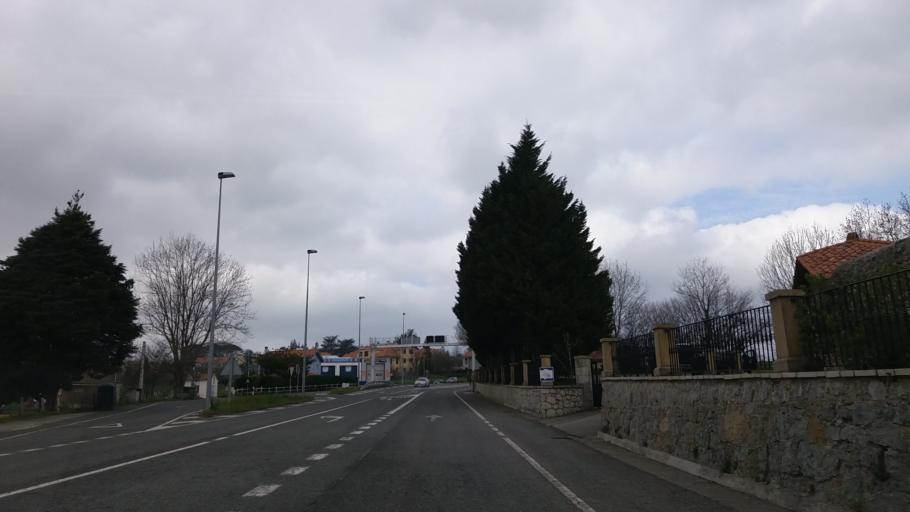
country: ES
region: Cantabria
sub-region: Provincia de Cantabria
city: Reocin
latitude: 43.3511
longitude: -4.1251
